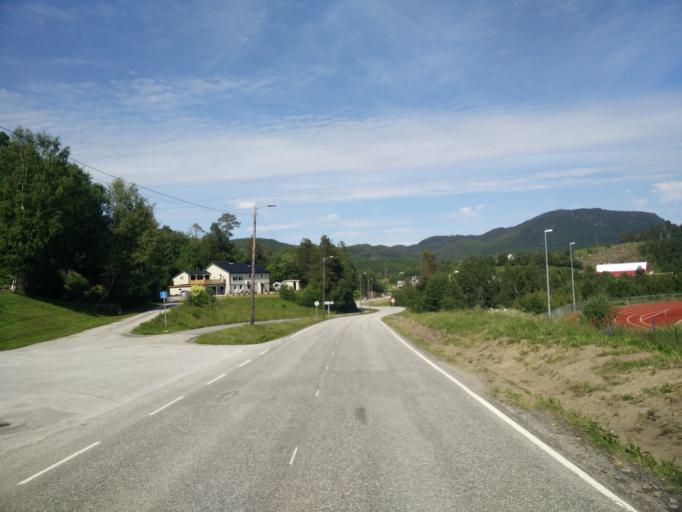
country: NO
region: More og Romsdal
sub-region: Tingvoll
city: Tingvoll
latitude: 63.0361
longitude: 8.0414
